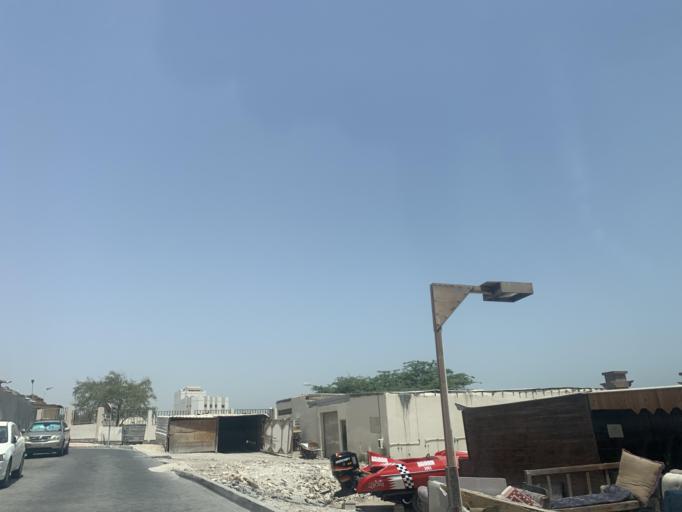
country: BH
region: Manama
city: Jidd Hafs
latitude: 26.2229
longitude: 50.5405
